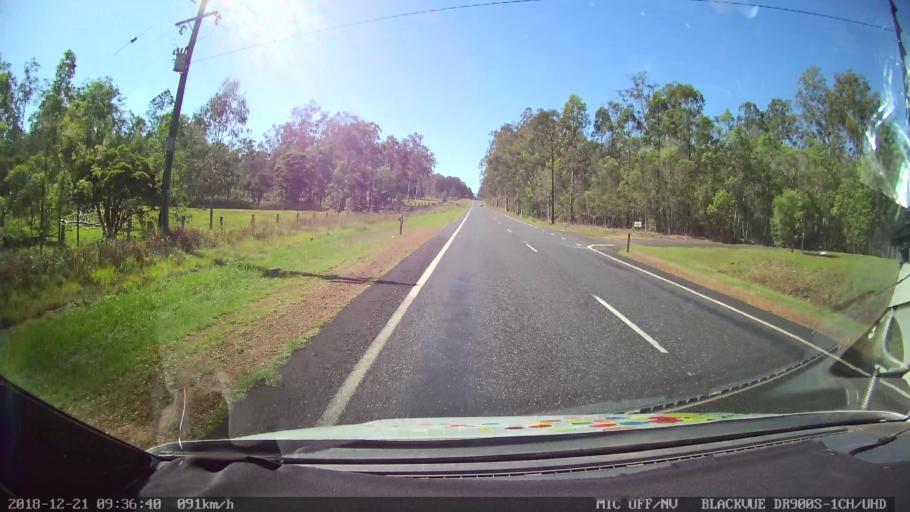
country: AU
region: New South Wales
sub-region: Clarence Valley
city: Grafton
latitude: -29.5264
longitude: 152.9840
